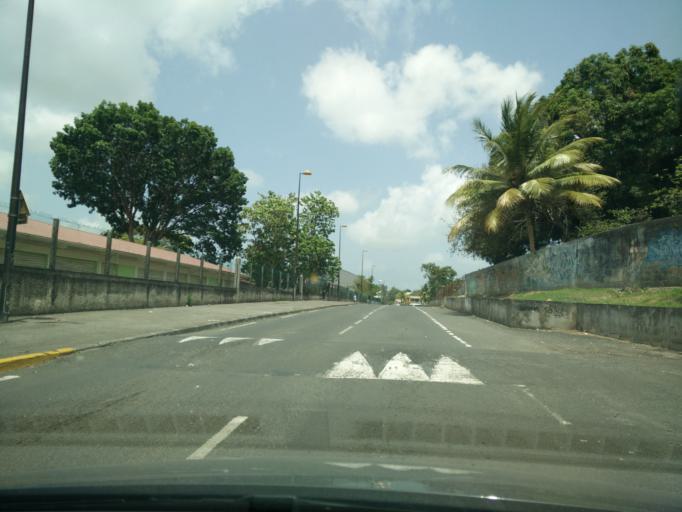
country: GP
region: Guadeloupe
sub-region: Guadeloupe
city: Les Abymes
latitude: 16.2782
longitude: -61.5034
